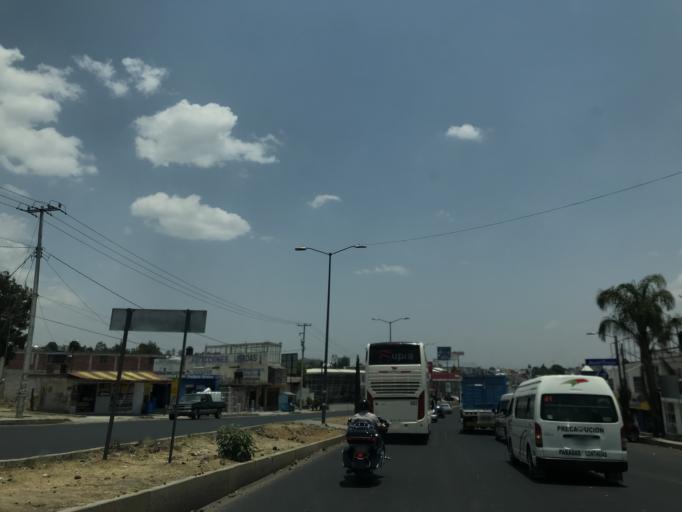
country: MX
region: Tlaxcala
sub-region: Yauhquemehcan
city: Hualcaltzinco
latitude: 19.4154
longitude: -98.1591
